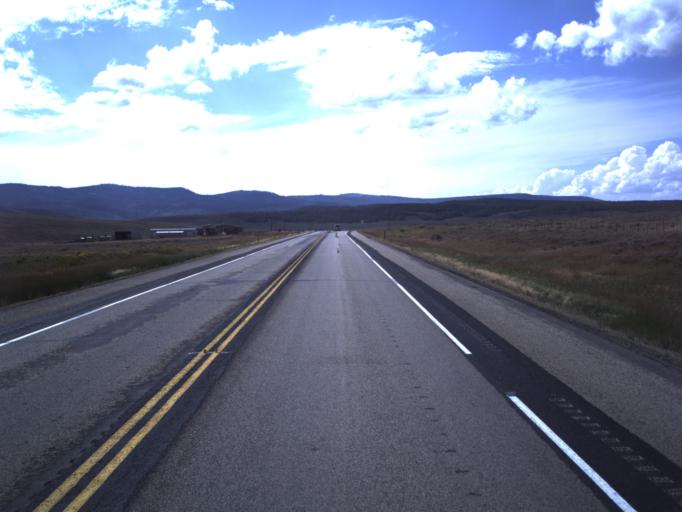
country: US
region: Utah
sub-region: Wasatch County
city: Heber
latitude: 40.2398
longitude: -111.1457
